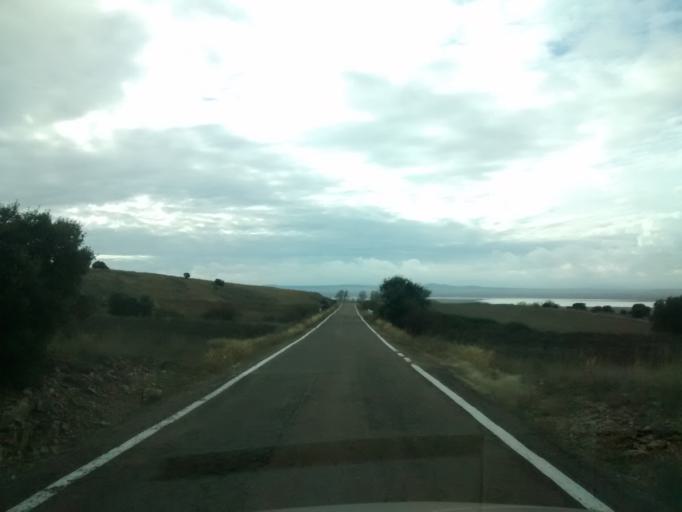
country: ES
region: Aragon
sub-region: Provincia de Teruel
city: Tornos
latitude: 40.9845
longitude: -1.4670
